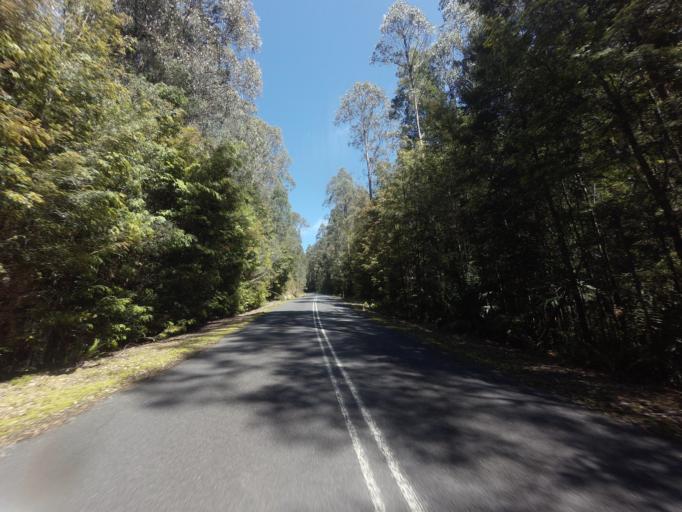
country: AU
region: Tasmania
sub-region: Huon Valley
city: Geeveston
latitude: -42.8238
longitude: 146.3321
